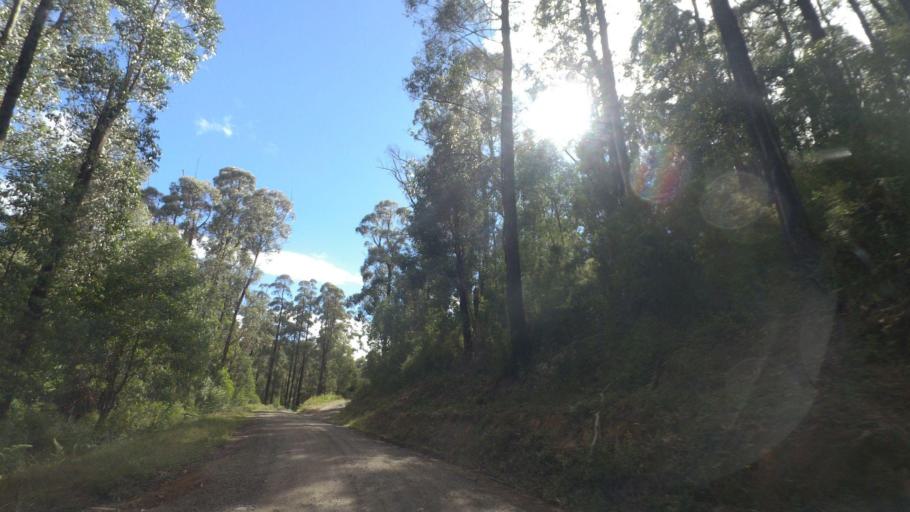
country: AU
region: Victoria
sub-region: Cardinia
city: Bunyip
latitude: -37.9761
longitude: 145.8147
